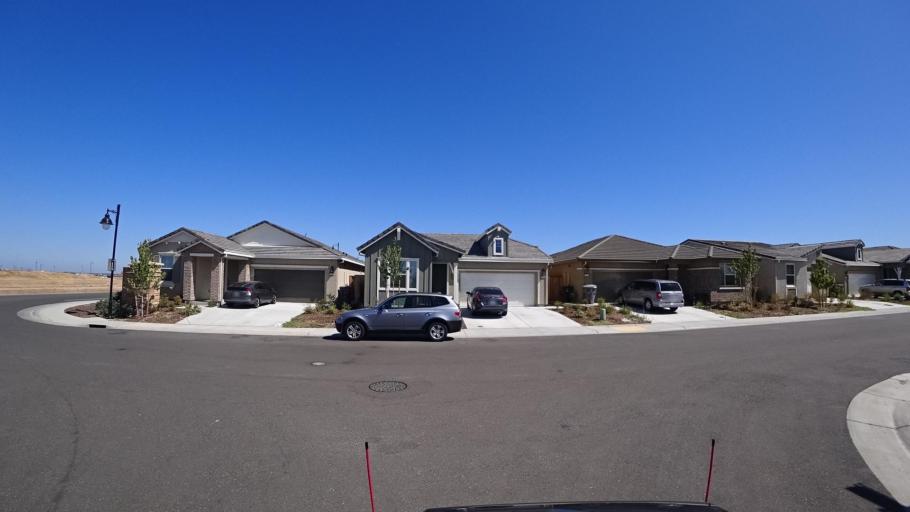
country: US
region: California
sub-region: Placer County
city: Lincoln
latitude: 38.8288
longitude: -121.2903
